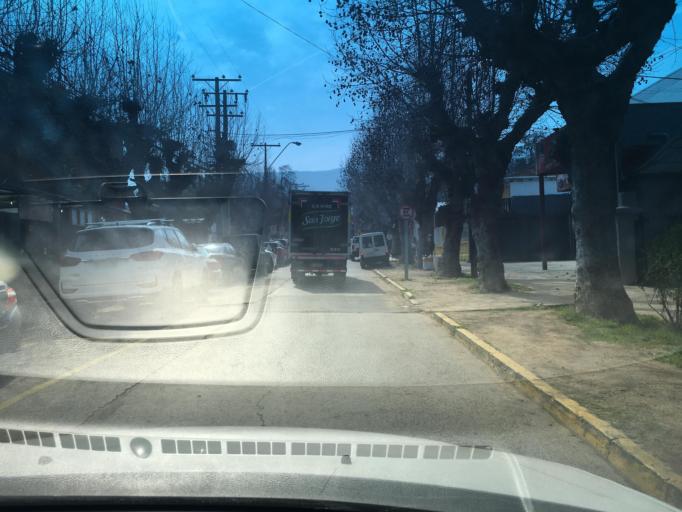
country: CL
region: Valparaiso
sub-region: Provincia de Marga Marga
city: Limache
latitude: -32.9861
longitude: -71.2762
